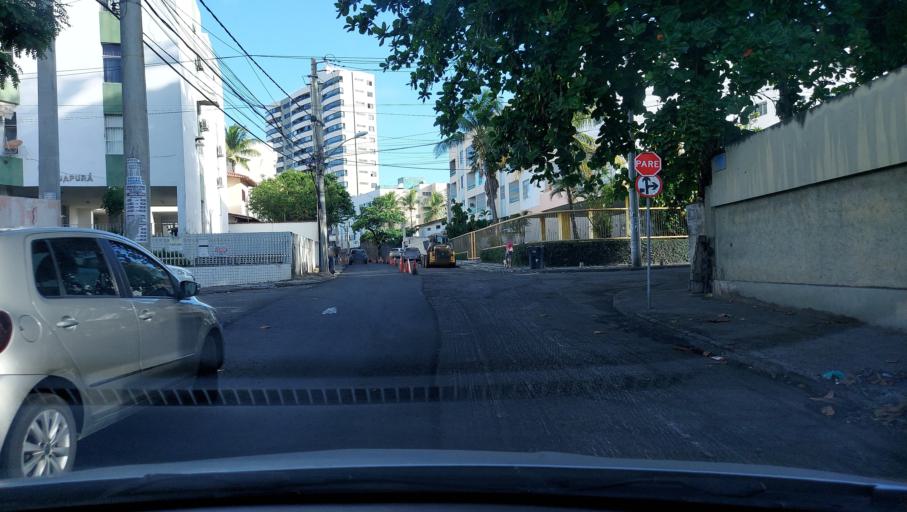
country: BR
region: Bahia
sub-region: Salvador
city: Salvador
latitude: -12.9951
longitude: -38.4473
